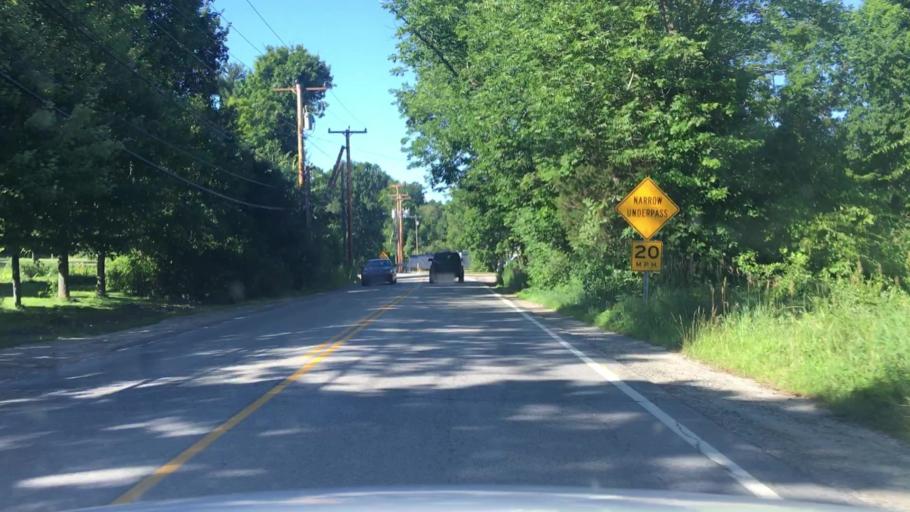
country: US
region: New Hampshire
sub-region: Rockingham County
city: Exeter
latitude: 42.9950
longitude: -70.9465
